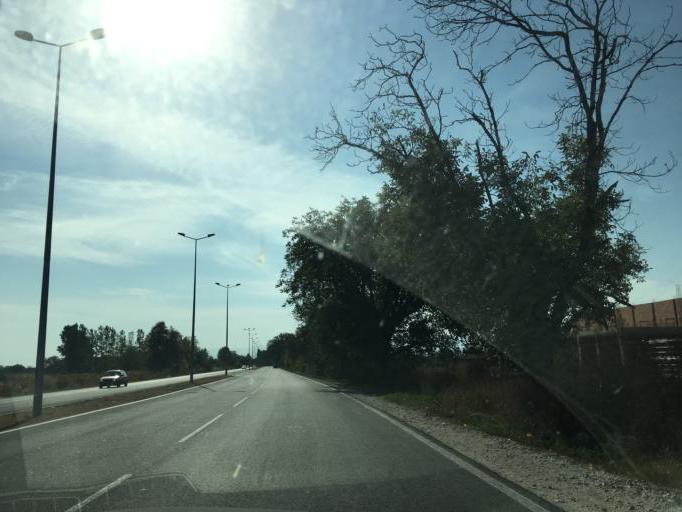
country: BG
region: Pazardzhik
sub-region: Obshtina Pazardzhik
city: Pazardzhik
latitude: 42.2208
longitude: 24.3122
